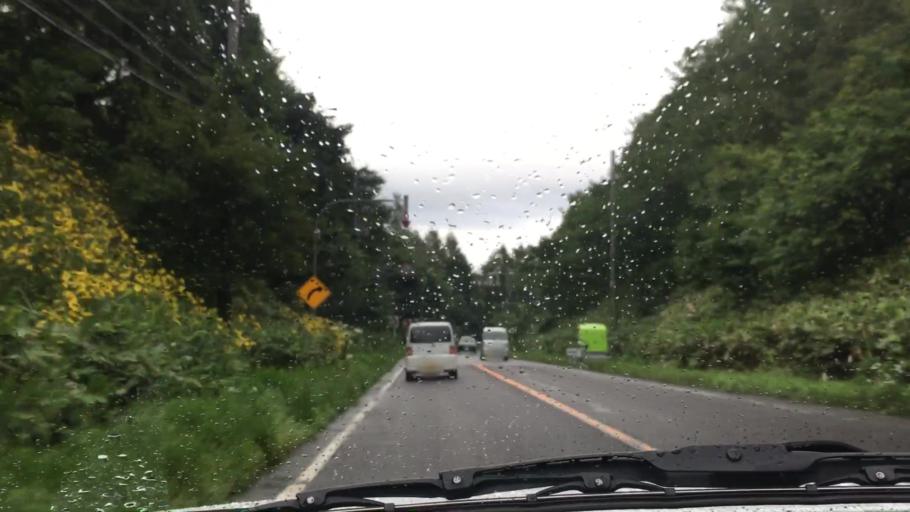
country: JP
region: Hokkaido
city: Niseko Town
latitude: 42.5941
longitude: 140.7207
